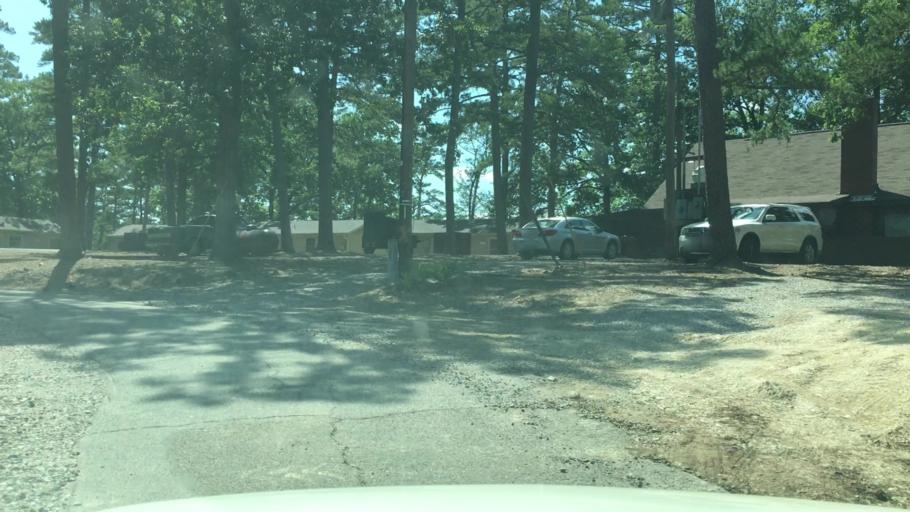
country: US
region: Arkansas
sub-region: Garland County
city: Piney
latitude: 34.5466
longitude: -93.3617
